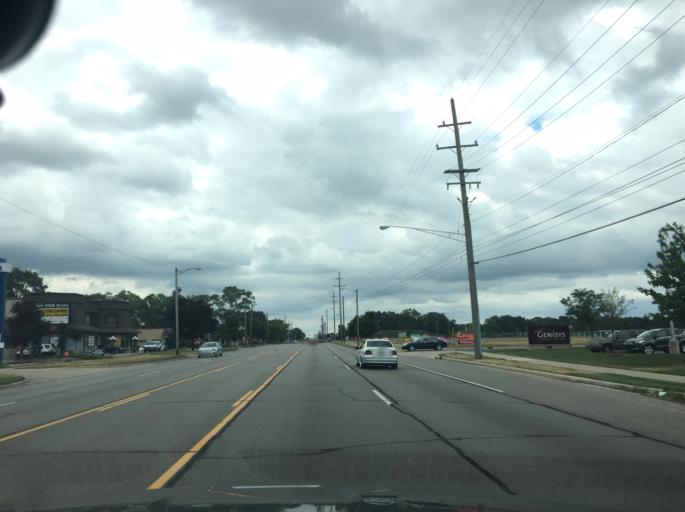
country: US
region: Michigan
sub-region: Macomb County
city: Shelby
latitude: 42.6599
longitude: -83.0336
